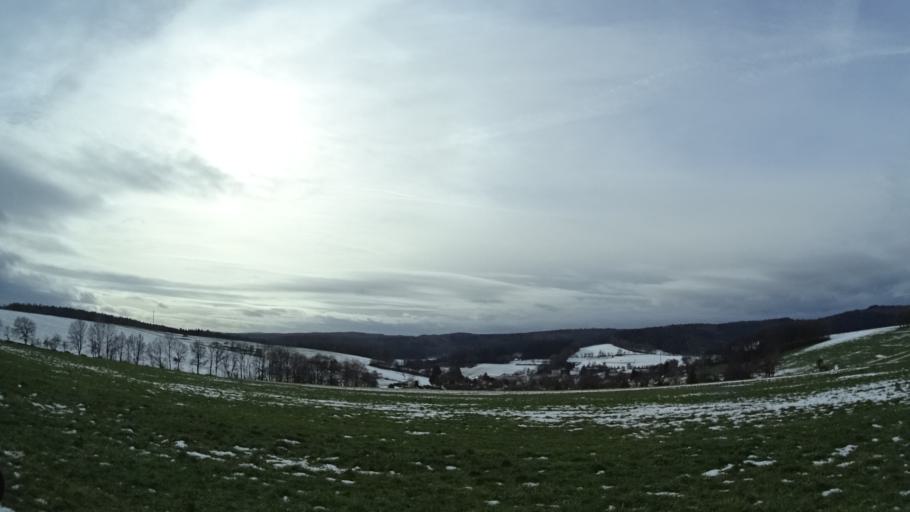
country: DE
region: Hesse
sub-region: Regierungsbezirk Darmstadt
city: Erbach
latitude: 49.6782
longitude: 8.9387
